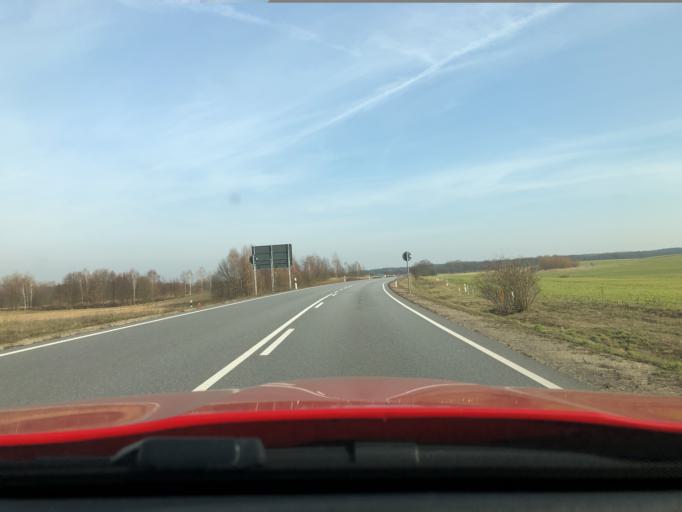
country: DE
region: Brandenburg
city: Muncheberg
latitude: 52.4934
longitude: 14.1586
